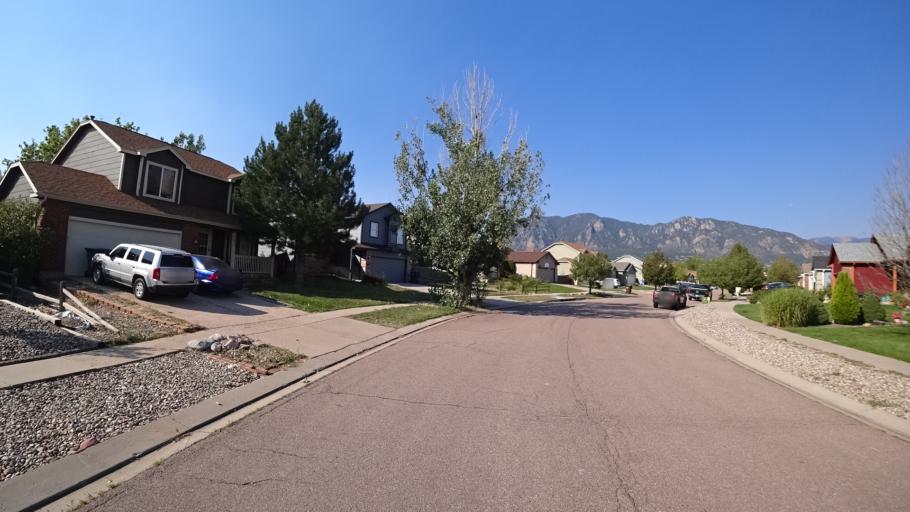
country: US
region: Colorado
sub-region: El Paso County
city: Stratmoor
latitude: 38.7688
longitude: -104.7995
